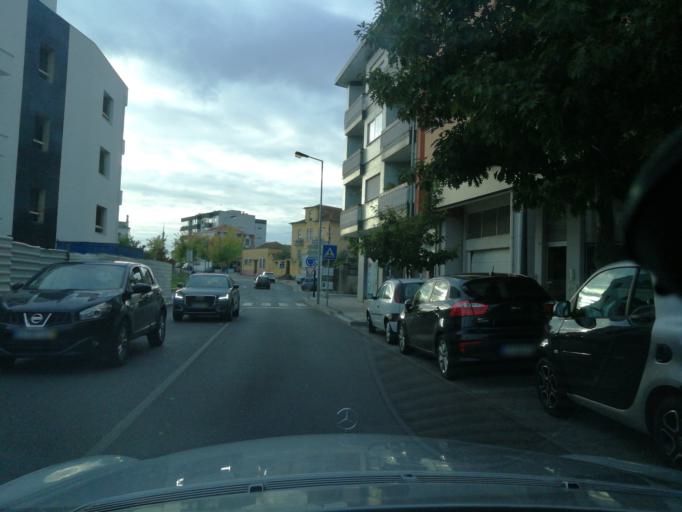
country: PT
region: Aveiro
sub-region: Agueda
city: Agueda
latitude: 40.5763
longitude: -8.4476
